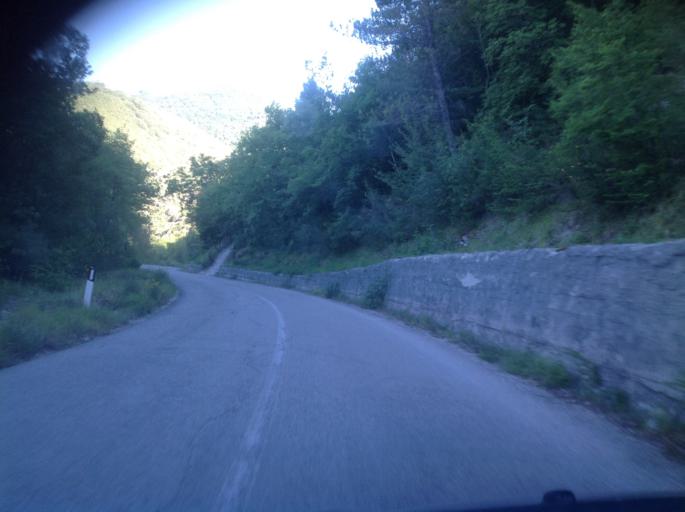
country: IT
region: Umbria
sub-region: Provincia di Terni
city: Stroncone
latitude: 42.4877
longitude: 12.6660
